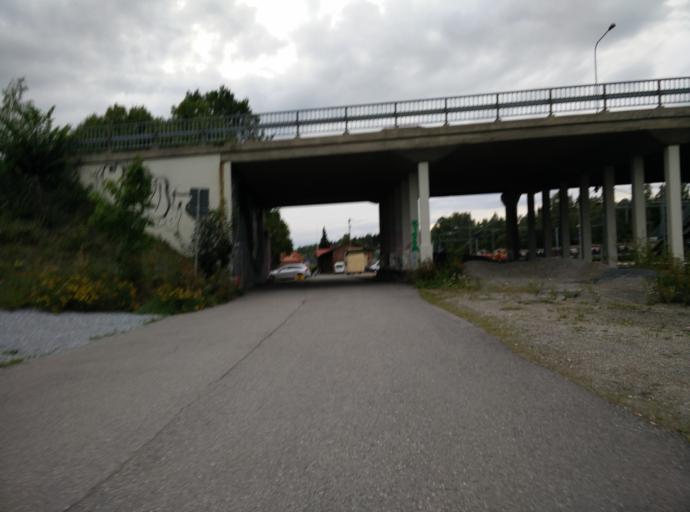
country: FI
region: Haeme
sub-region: Haemeenlinna
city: Haemeenlinna
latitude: 61.0003
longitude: 24.4823
